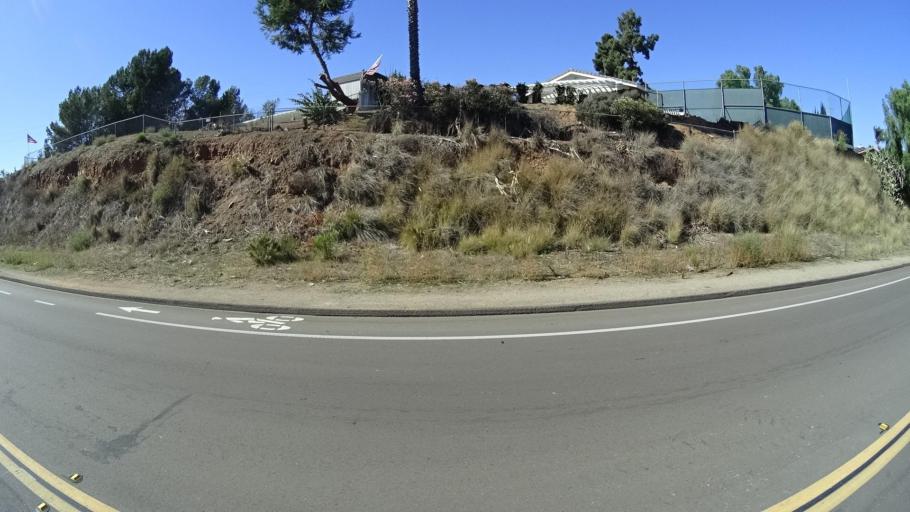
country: US
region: California
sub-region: San Diego County
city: Bonita
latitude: 32.6808
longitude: -117.0147
